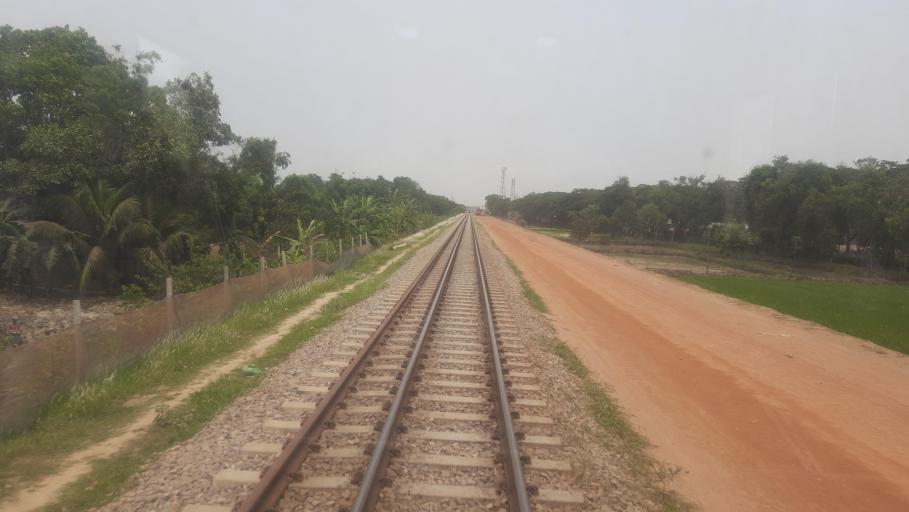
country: BD
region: Chittagong
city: Comilla
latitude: 23.6281
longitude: 91.1471
